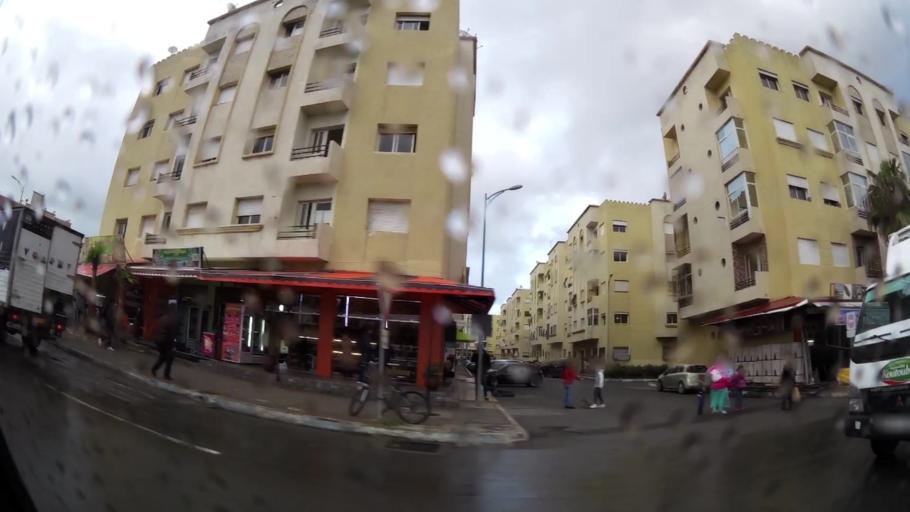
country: MA
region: Grand Casablanca
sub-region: Mohammedia
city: Mohammedia
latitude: 33.6789
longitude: -7.4007
